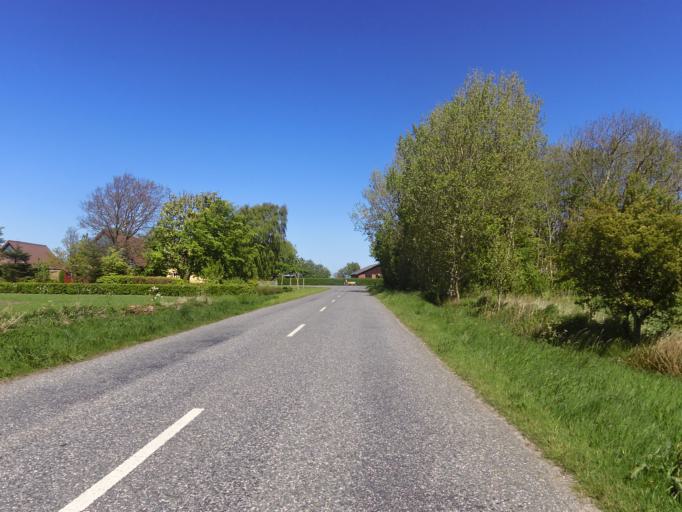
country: DK
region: South Denmark
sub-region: Tonder Kommune
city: Sherrebek
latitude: 55.2332
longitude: 8.7177
